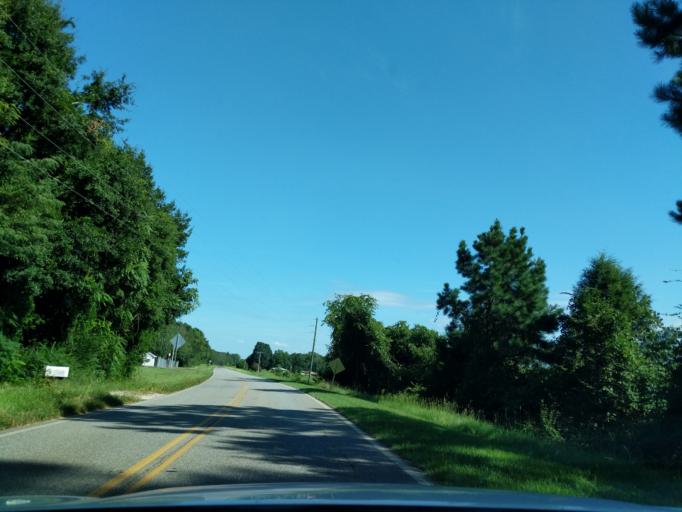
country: US
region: Georgia
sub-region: Oglethorpe County
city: Lexington
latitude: 33.9091
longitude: -83.0064
